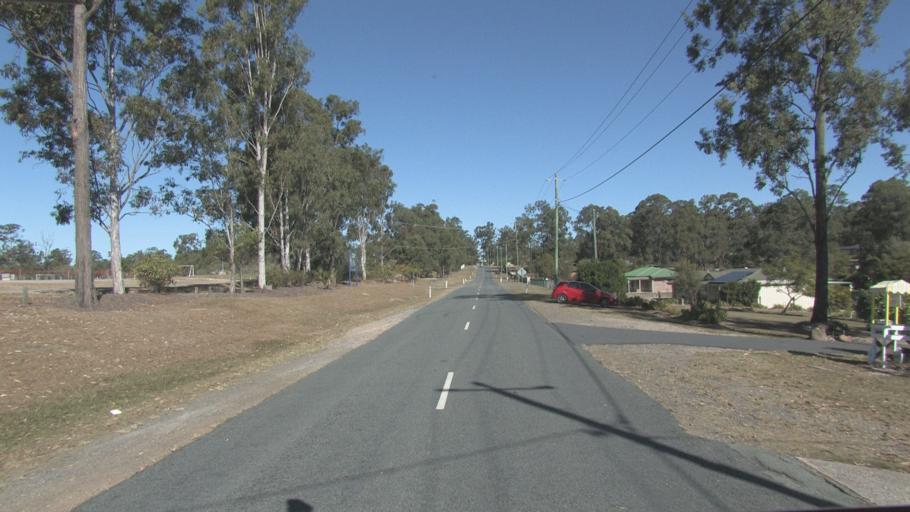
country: AU
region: Queensland
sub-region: Logan
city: North Maclean
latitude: -27.7272
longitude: 152.9621
